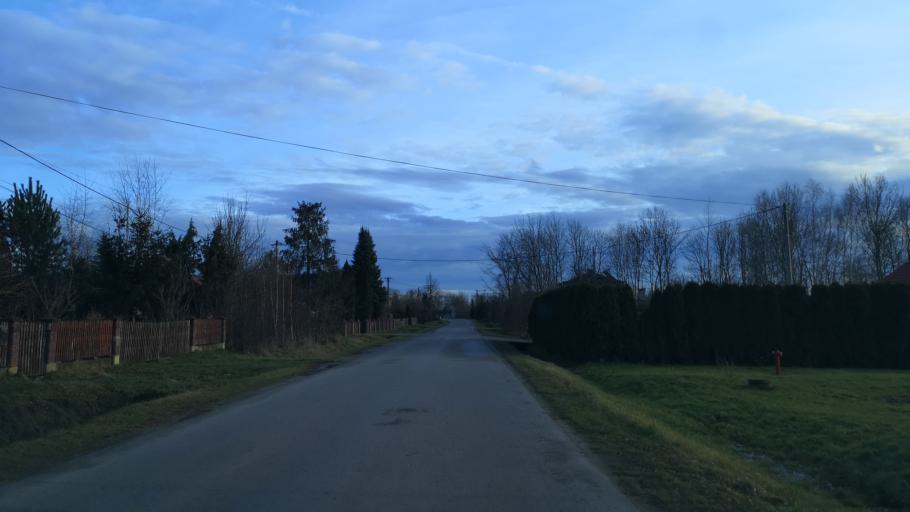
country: PL
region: Subcarpathian Voivodeship
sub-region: Powiat przeworski
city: Adamowka
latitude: 50.2427
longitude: 22.6369
